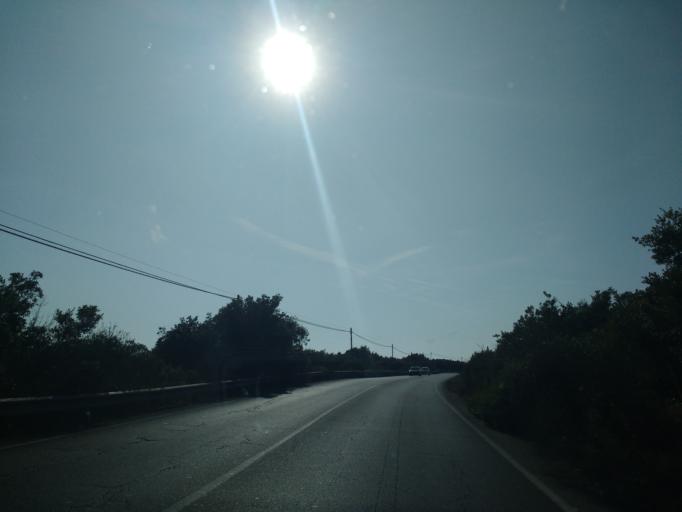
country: IT
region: Latium
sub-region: Citta metropolitana di Roma Capitale
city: Acilia-Castel Fusano-Ostia Antica
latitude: 41.6957
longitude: 12.3612
